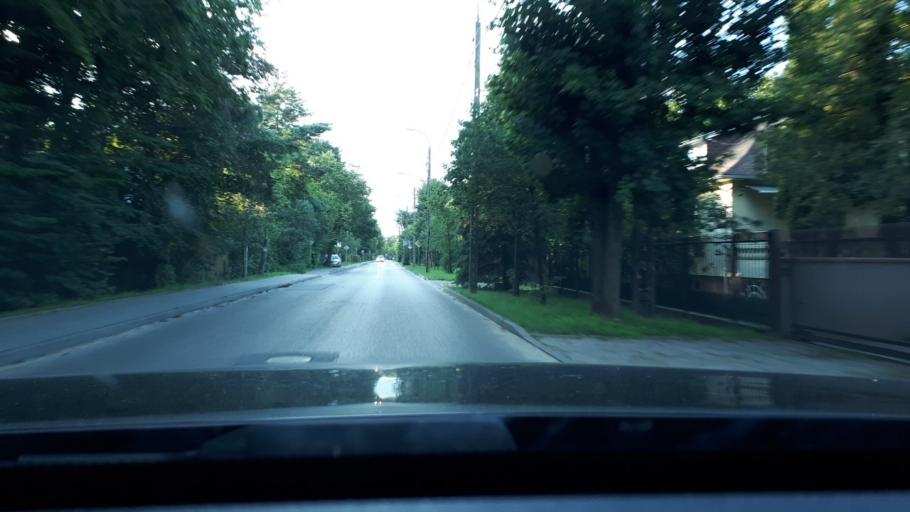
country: PL
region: Masovian Voivodeship
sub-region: Powiat pruszkowski
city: Komorow
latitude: 52.1486
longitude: 20.8096
